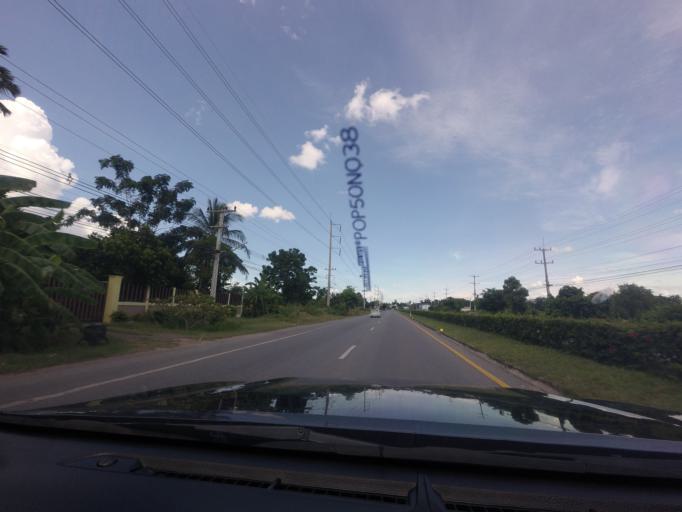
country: TH
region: Kanchanaburi
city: Kanchanaburi
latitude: 14.0446
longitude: 99.6159
